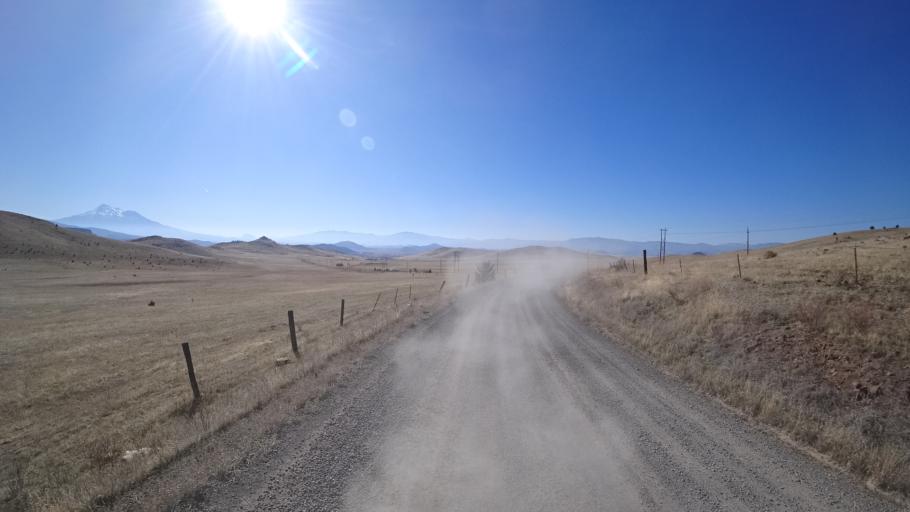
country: US
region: California
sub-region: Siskiyou County
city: Montague
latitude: 41.7634
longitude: -122.3573
